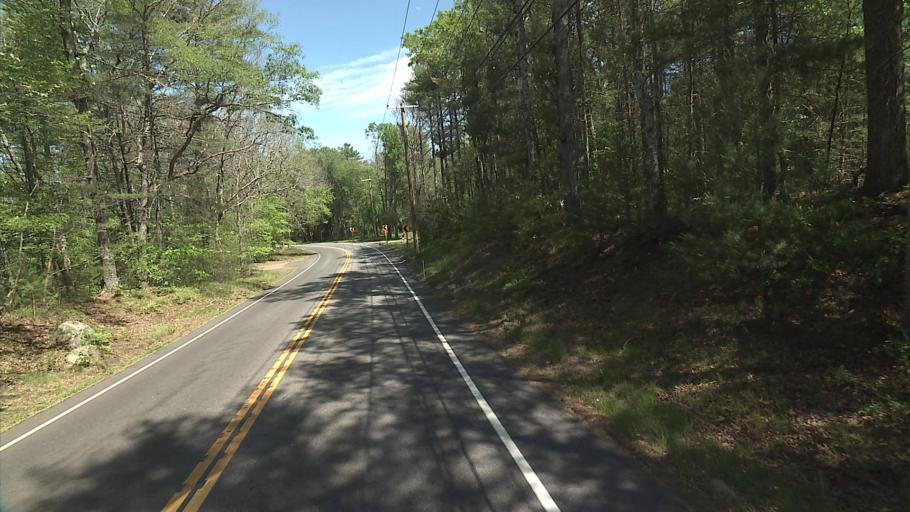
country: US
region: Connecticut
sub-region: Windham County
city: Plainfield
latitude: 41.5683
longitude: -71.8579
